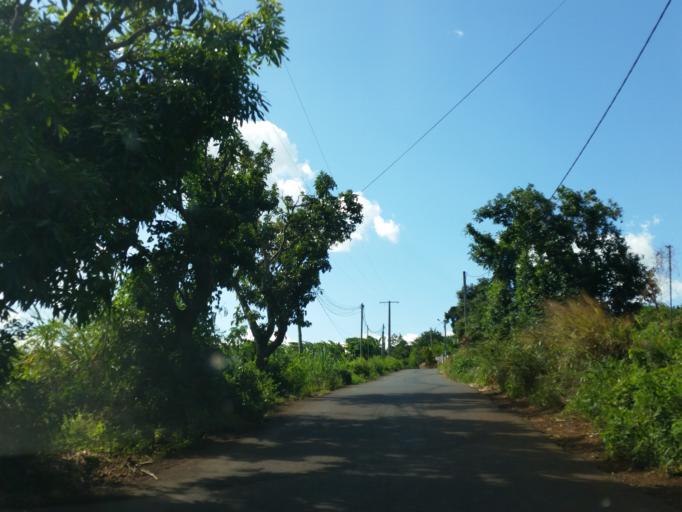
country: RE
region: Reunion
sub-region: Reunion
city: Saint-Pierre
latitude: -21.3226
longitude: 55.5010
